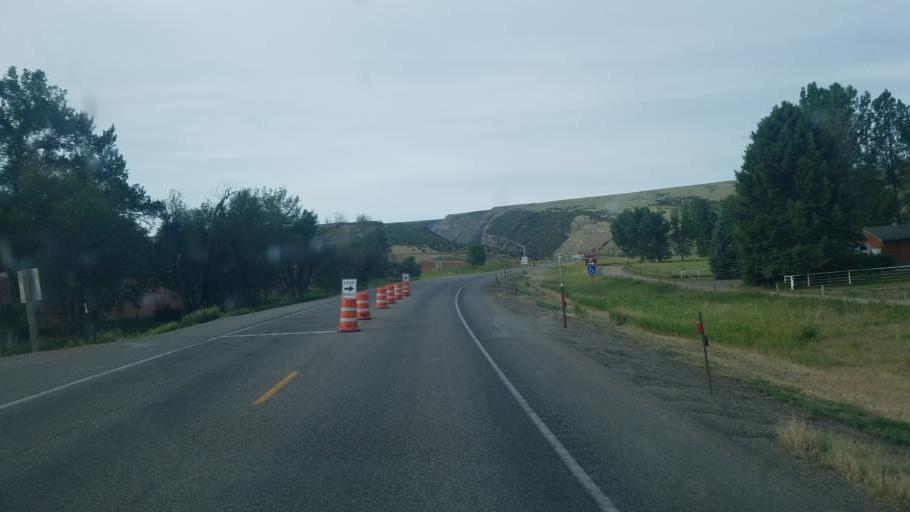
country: US
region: Wyoming
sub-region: Hot Springs County
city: Thermopolis
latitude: 43.5906
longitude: -108.2130
